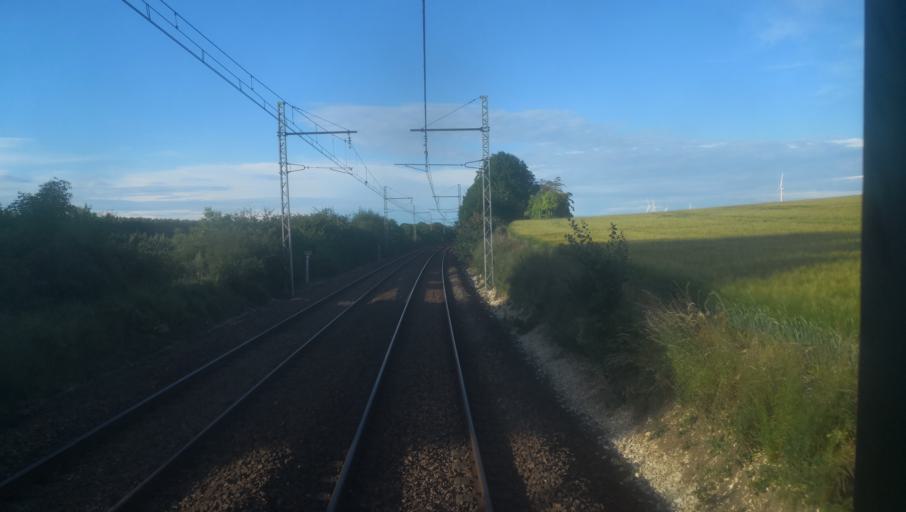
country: FR
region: Centre
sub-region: Departement de l'Indre
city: Sainte-Lizaigne
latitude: 46.9806
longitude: 2.0101
